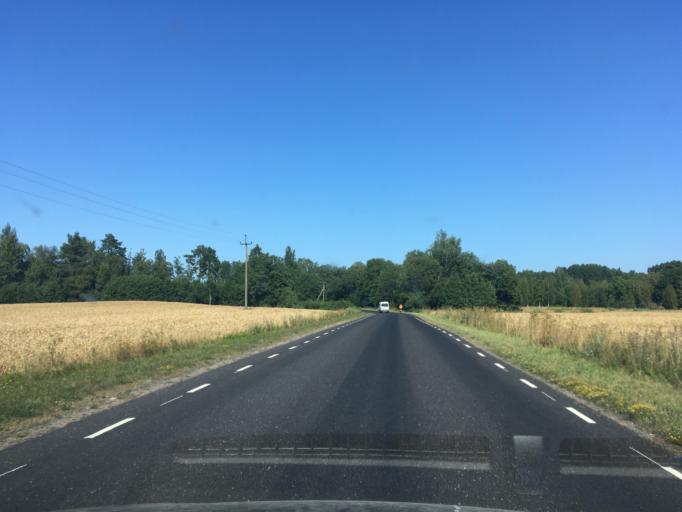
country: EE
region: Harju
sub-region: Anija vald
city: Kehra
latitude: 59.1631
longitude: 25.2131
